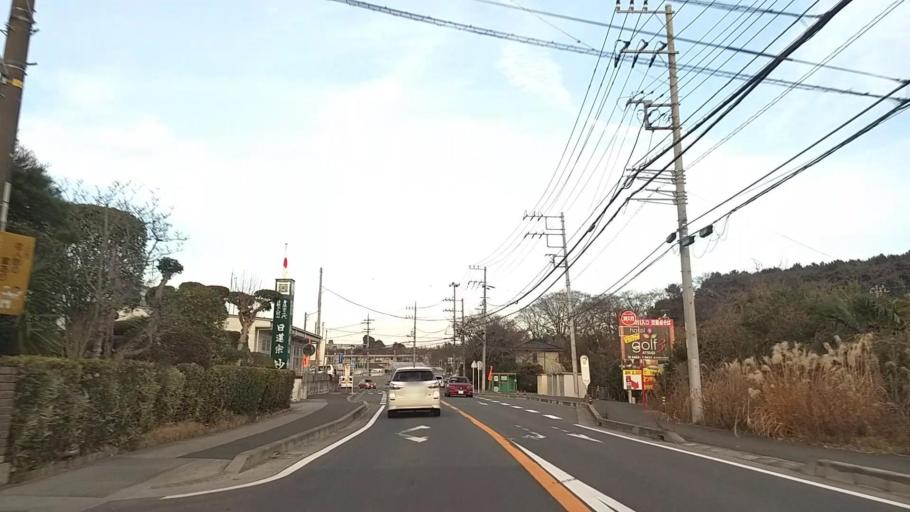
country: JP
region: Kanagawa
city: Atsugi
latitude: 35.4452
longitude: 139.3265
